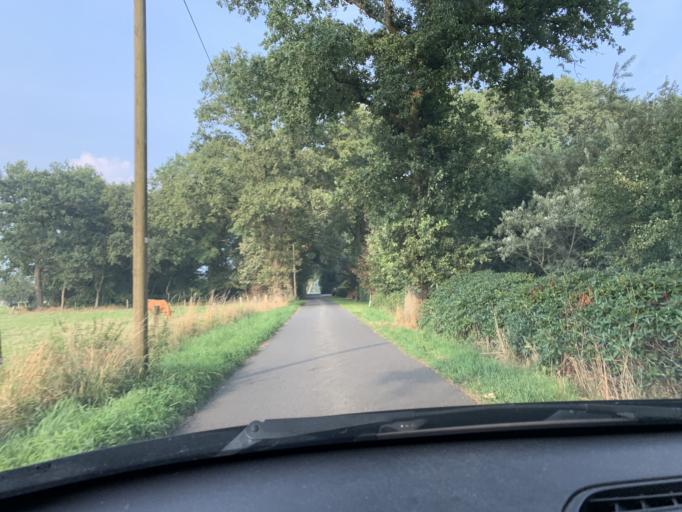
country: DE
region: Lower Saxony
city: Apen
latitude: 53.2464
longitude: 7.8284
